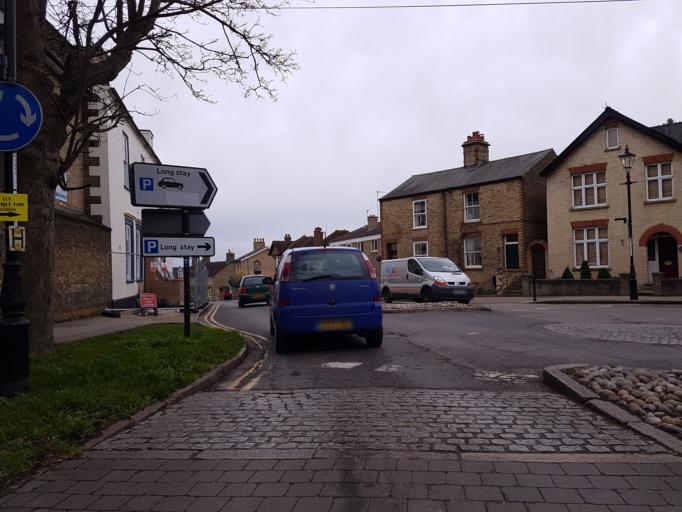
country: GB
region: England
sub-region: Cambridgeshire
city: Ely
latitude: 52.3960
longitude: 0.2620
